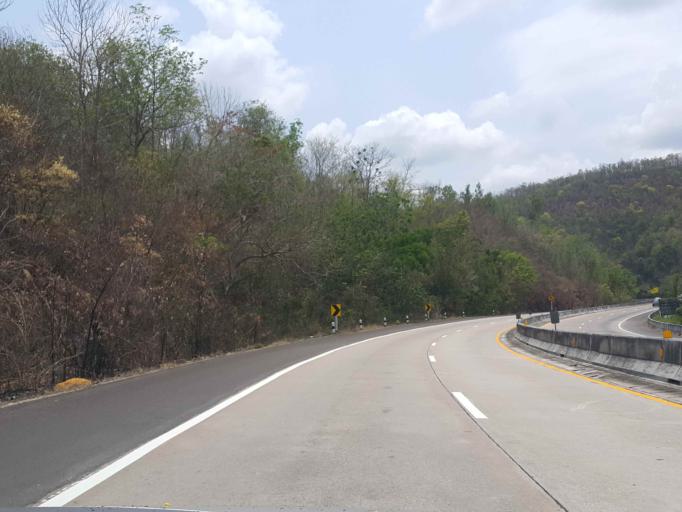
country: TH
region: Lampang
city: Hang Chat
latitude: 18.3316
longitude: 99.2528
